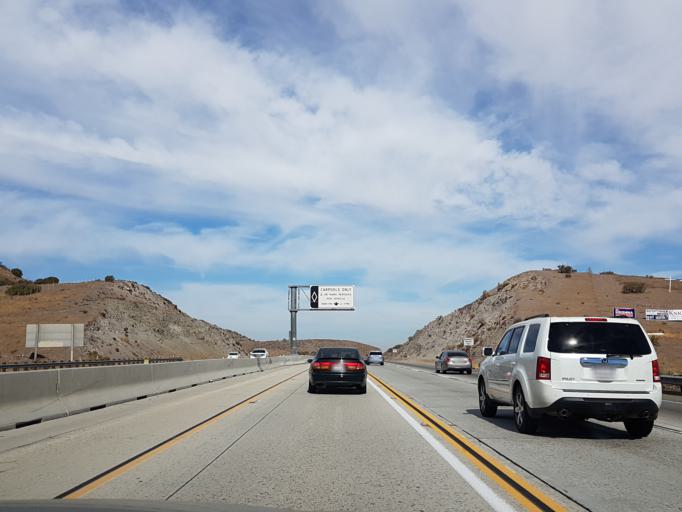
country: US
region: California
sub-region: Los Angeles County
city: Vincent
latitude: 34.5232
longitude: -118.1115
